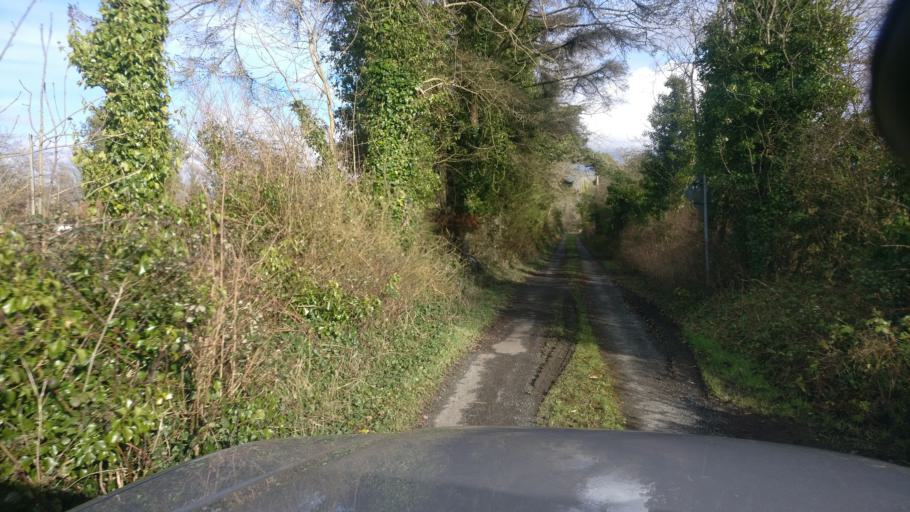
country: IE
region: Connaught
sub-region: County Galway
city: Loughrea
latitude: 53.1821
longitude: -8.4265
